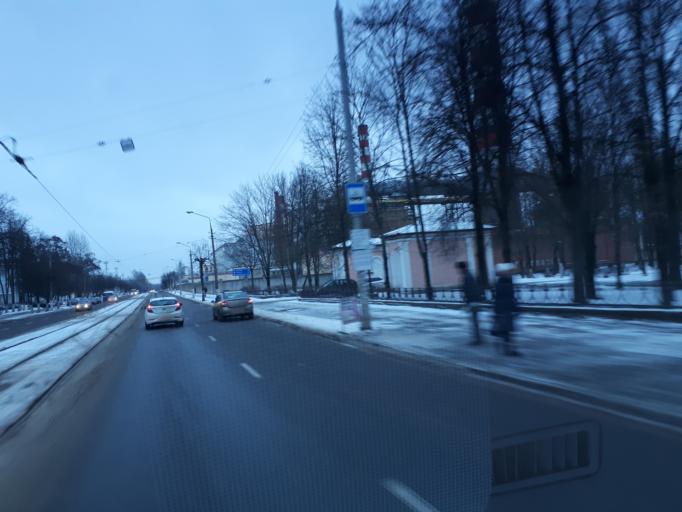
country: BY
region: Vitebsk
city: Vitebsk
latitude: 55.1677
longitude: 30.1303
